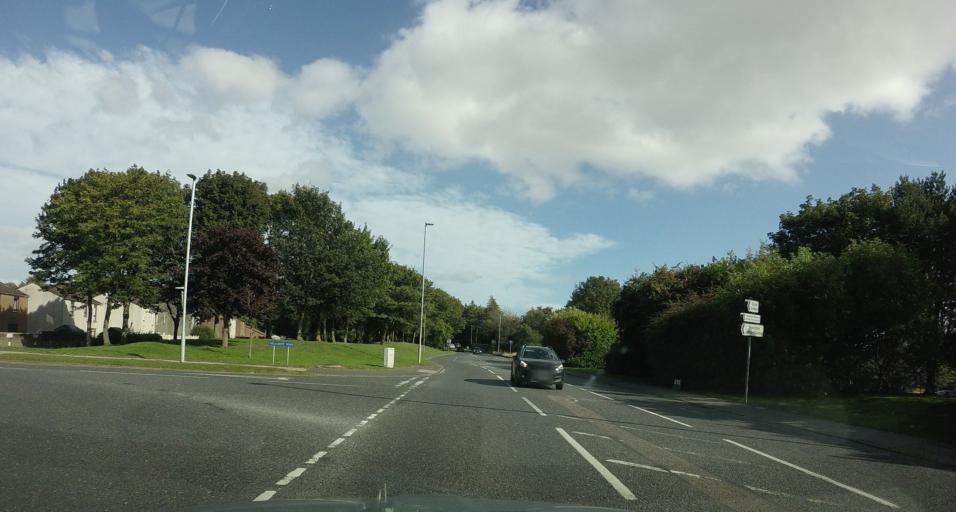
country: GB
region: Scotland
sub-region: Aberdeenshire
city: Westhill
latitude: 57.1493
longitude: -2.2918
